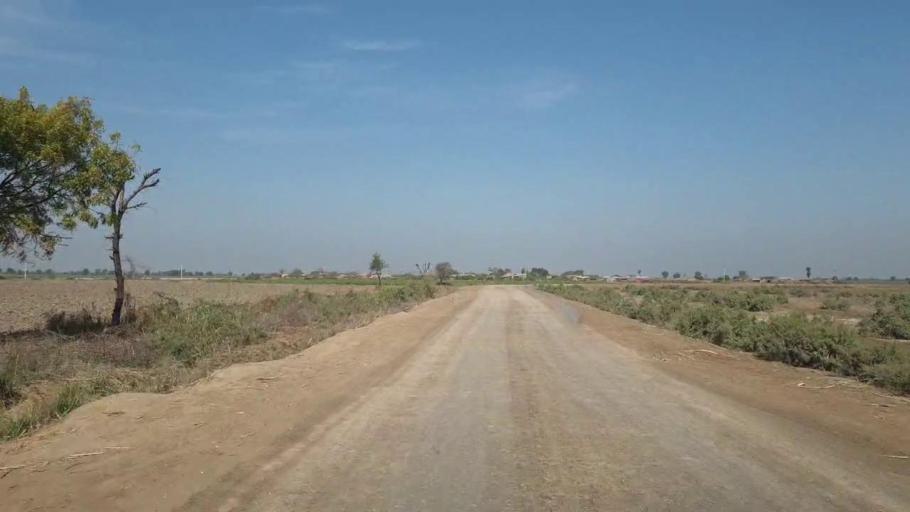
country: PK
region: Sindh
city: Samaro
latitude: 25.3416
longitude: 69.2484
